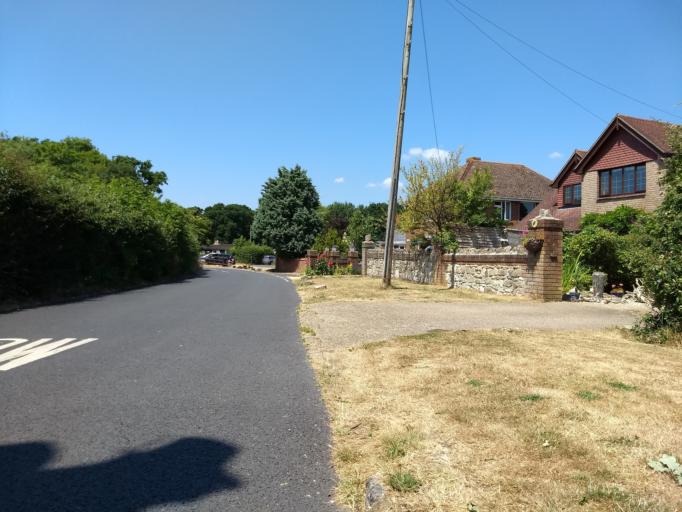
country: GB
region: England
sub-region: Isle of Wight
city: Shalfleet
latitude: 50.7183
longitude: -1.3683
